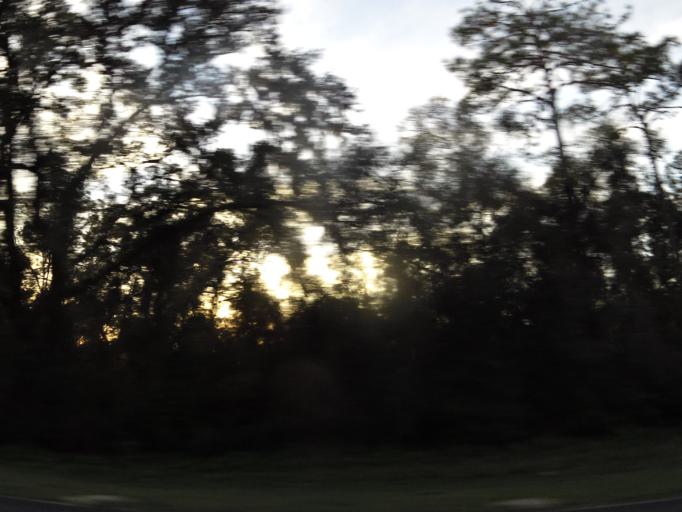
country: US
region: Florida
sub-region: Volusia County
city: De Leon Springs
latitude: 29.1340
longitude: -81.2850
